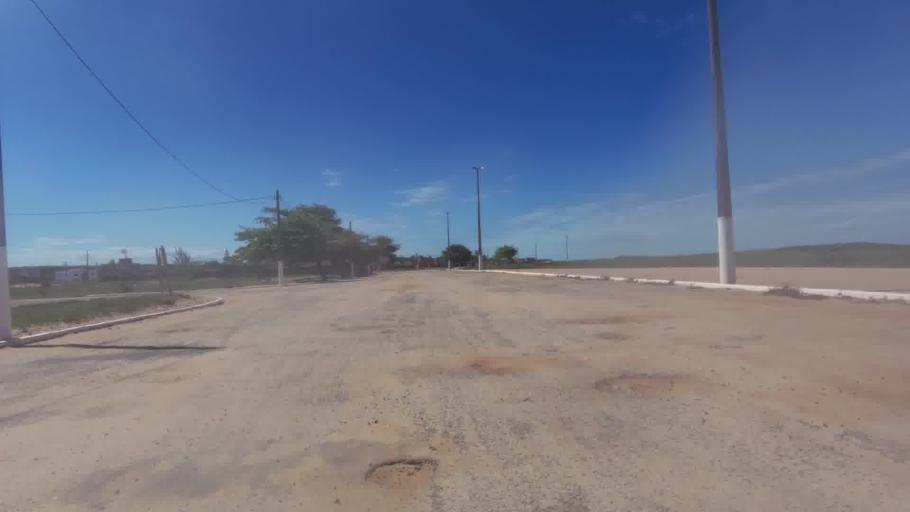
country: BR
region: Espirito Santo
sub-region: Marataizes
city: Marataizes
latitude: -21.1938
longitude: -40.9302
